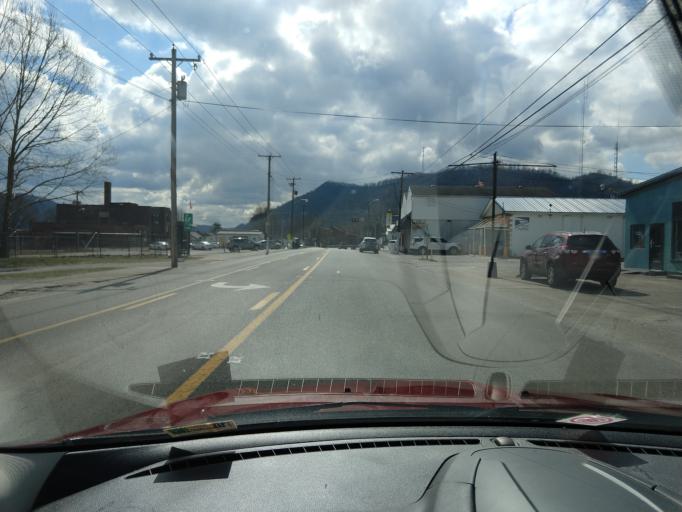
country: US
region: West Virginia
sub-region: Kanawha County
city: Marmet
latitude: 38.2465
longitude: -81.5680
